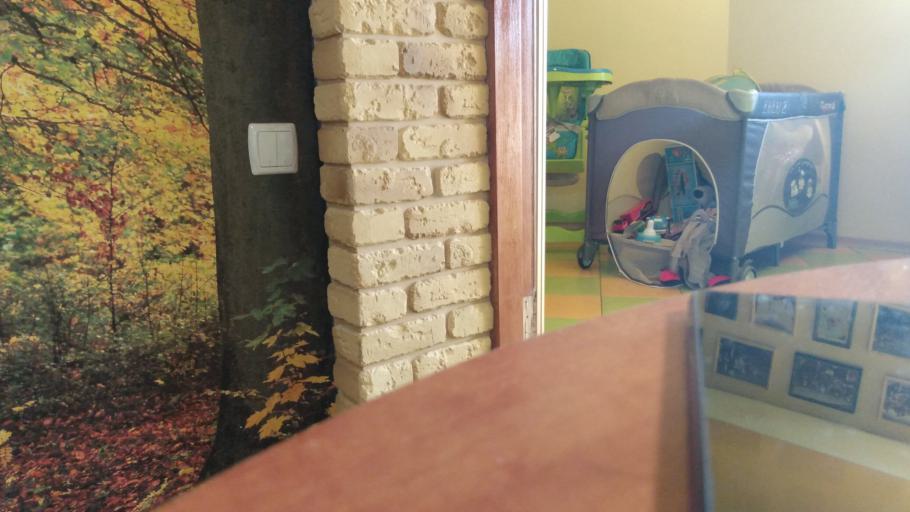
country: RU
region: Tverskaya
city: Bologoye
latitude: 57.8644
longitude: 34.3201
